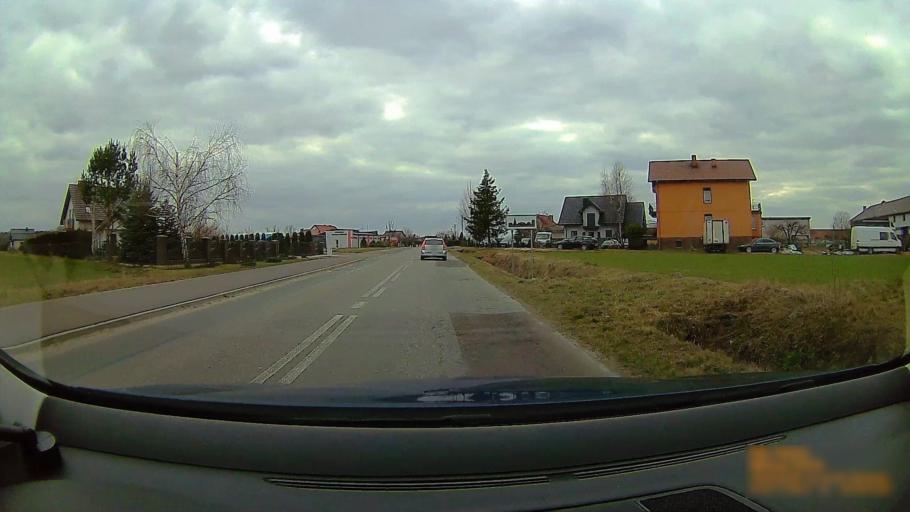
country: PL
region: Greater Poland Voivodeship
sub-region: Powiat koninski
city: Golina
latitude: 52.1905
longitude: 18.1178
